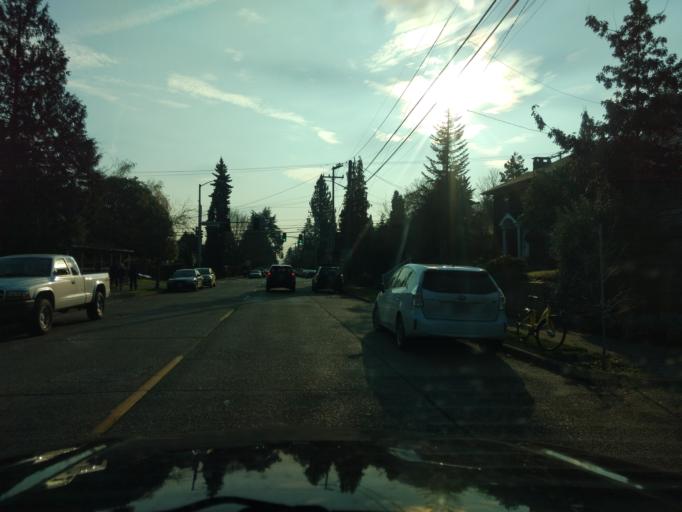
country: US
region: Washington
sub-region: King County
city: Lake Forest Park
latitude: 47.6836
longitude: -122.3068
